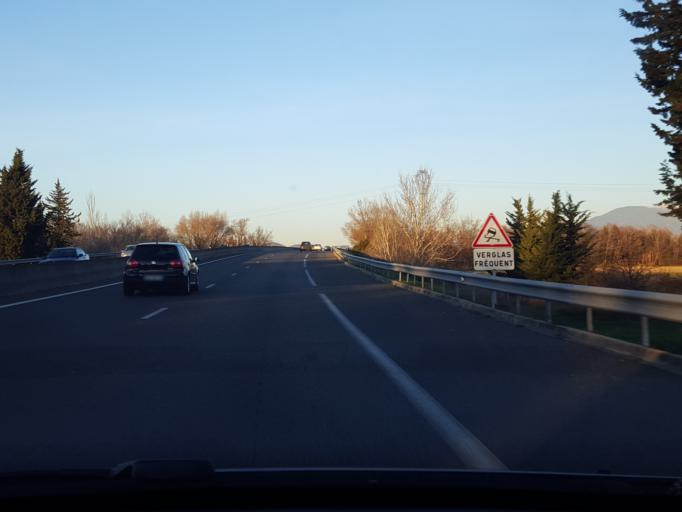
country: FR
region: Provence-Alpes-Cote d'Azur
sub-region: Departement du Vaucluse
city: Monteux
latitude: 44.0380
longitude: 4.9718
